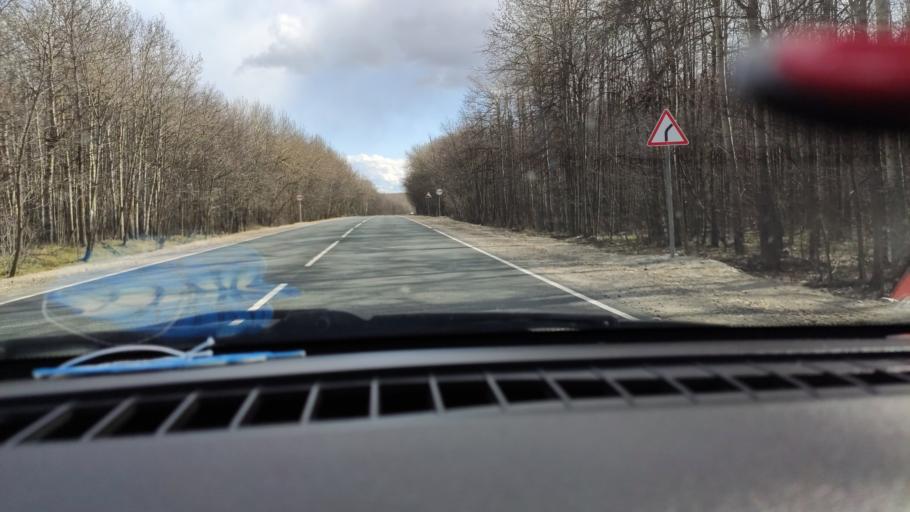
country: RU
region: Saratov
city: Khvalynsk
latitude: 52.4620
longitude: 48.0175
